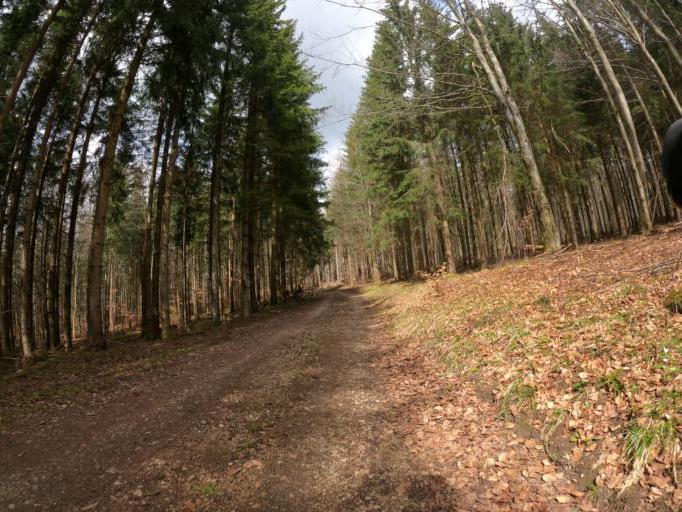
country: DE
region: Baden-Wuerttemberg
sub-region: Tuebingen Region
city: Trochtelfingen
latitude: 48.3798
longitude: 9.2314
